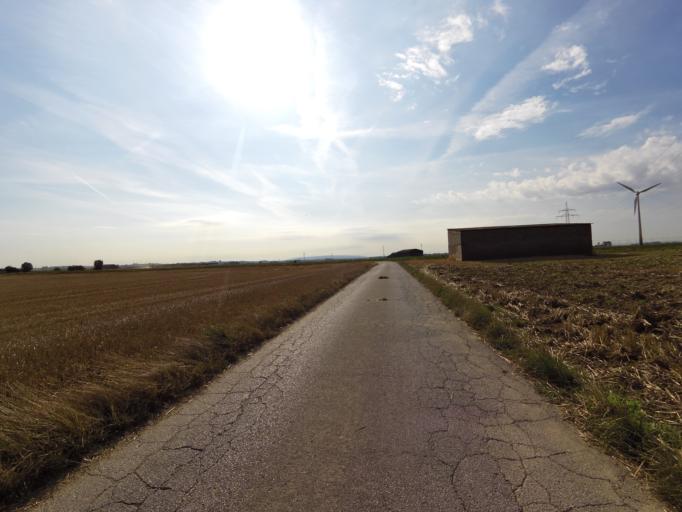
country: DE
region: North Rhine-Westphalia
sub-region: Regierungsbezirk Koln
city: Linnich
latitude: 50.9934
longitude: 6.2359
